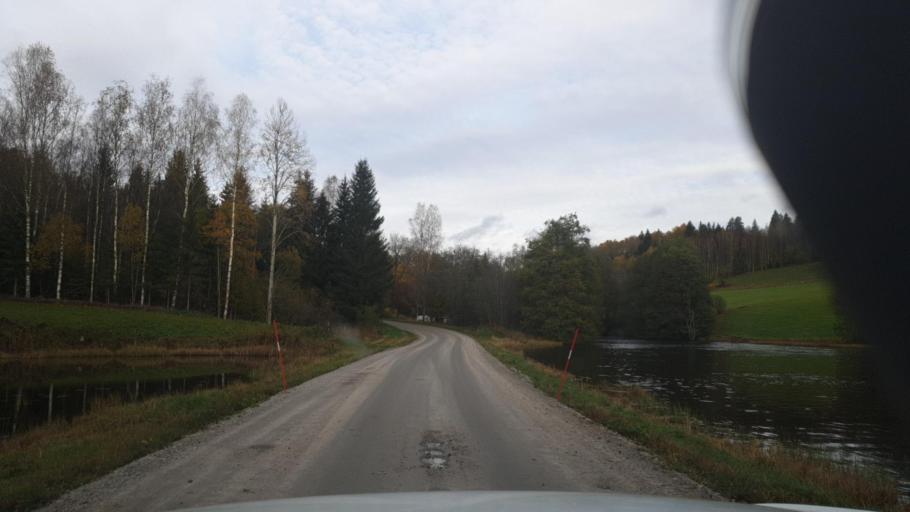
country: SE
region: Vaermland
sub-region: Sunne Kommun
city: Sunne
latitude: 59.6921
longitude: 12.8879
